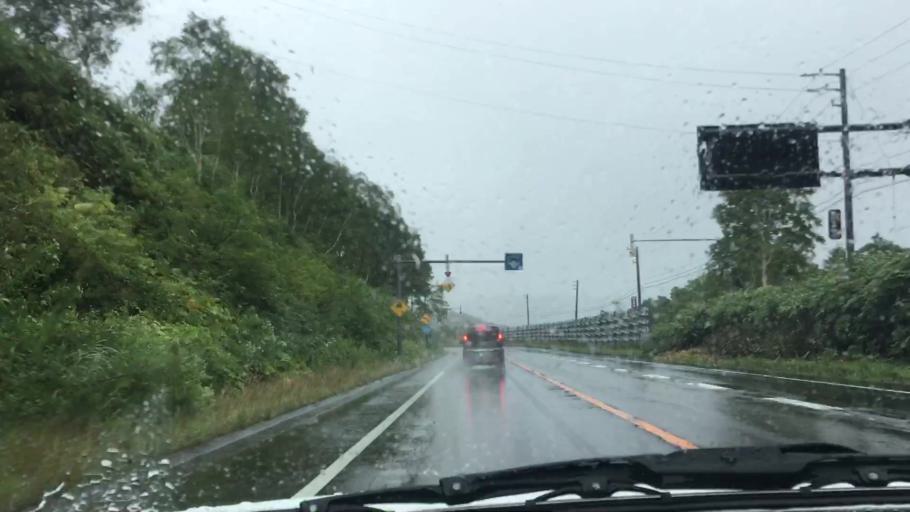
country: JP
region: Hokkaido
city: Sapporo
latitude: 42.8552
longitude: 141.0942
